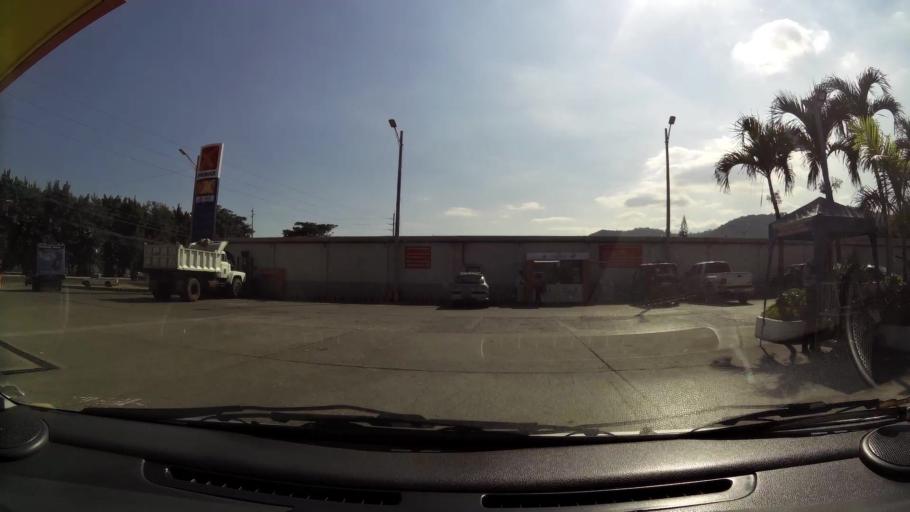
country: EC
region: Guayas
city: Santa Lucia
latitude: -2.1837
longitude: -79.9770
